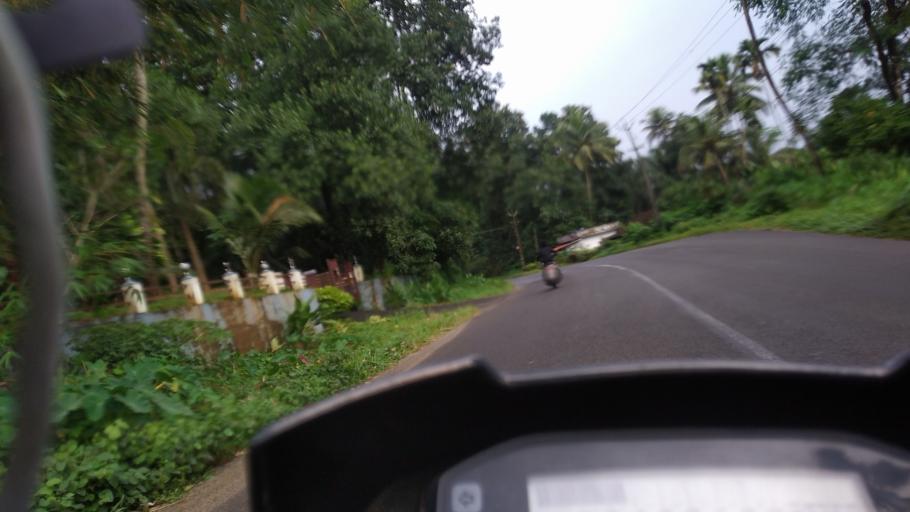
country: IN
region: Kerala
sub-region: Ernakulam
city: Kotamangalam
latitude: 10.0583
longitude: 76.6923
